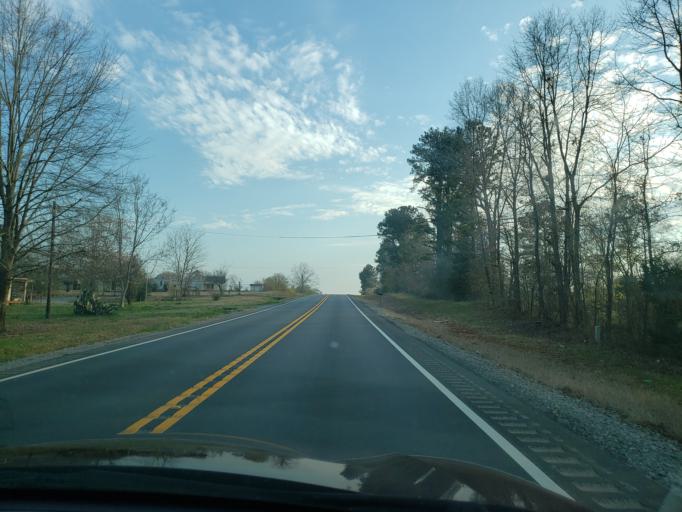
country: US
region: Alabama
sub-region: Hale County
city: Moundville
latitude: 32.8797
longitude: -87.6091
